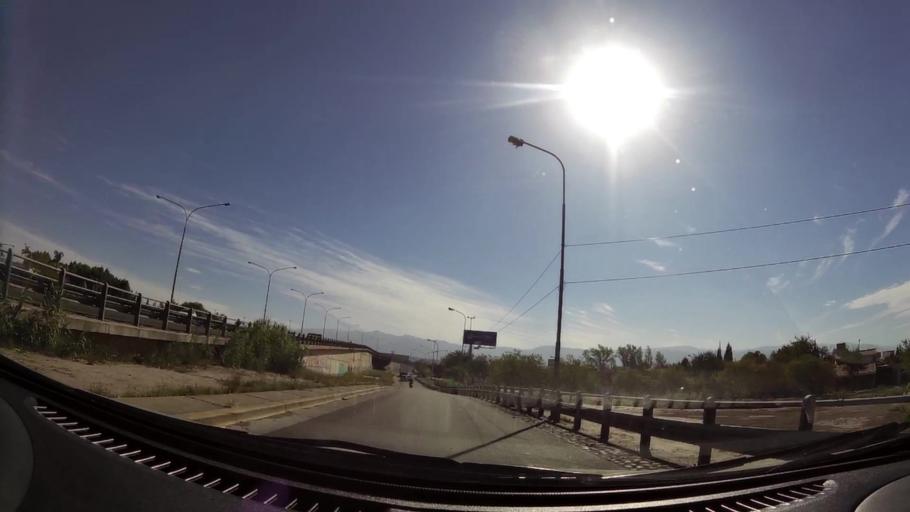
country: AR
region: Mendoza
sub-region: Departamento de Godoy Cruz
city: Godoy Cruz
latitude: -32.9254
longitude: -68.8307
